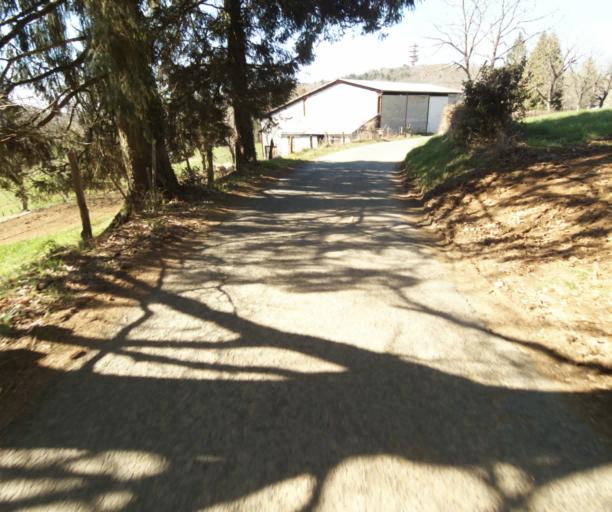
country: FR
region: Limousin
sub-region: Departement de la Correze
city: Seilhac
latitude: 45.3547
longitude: 1.7243
